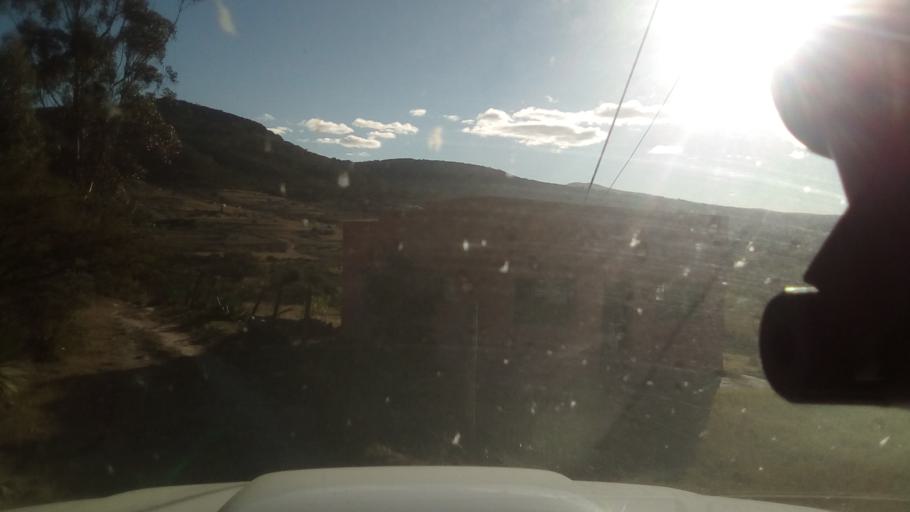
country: ZA
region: Eastern Cape
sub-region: Buffalo City Metropolitan Municipality
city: Bhisho
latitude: -32.7328
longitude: 27.3606
